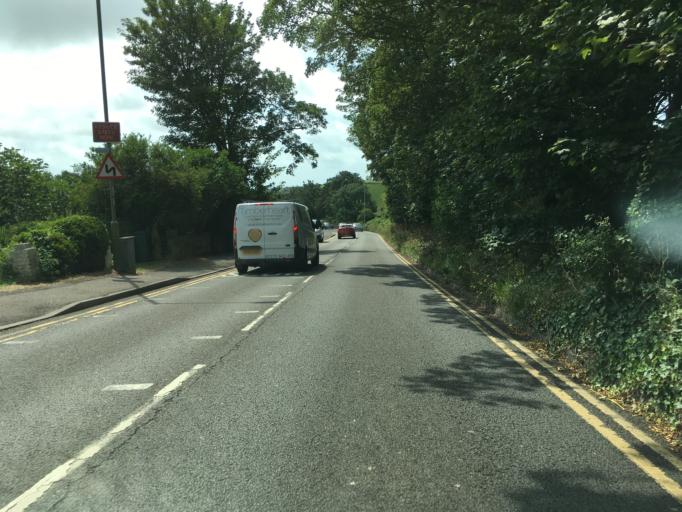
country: GB
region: England
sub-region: Brighton and Hove
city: Rottingdean
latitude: 50.8340
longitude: -0.0751
